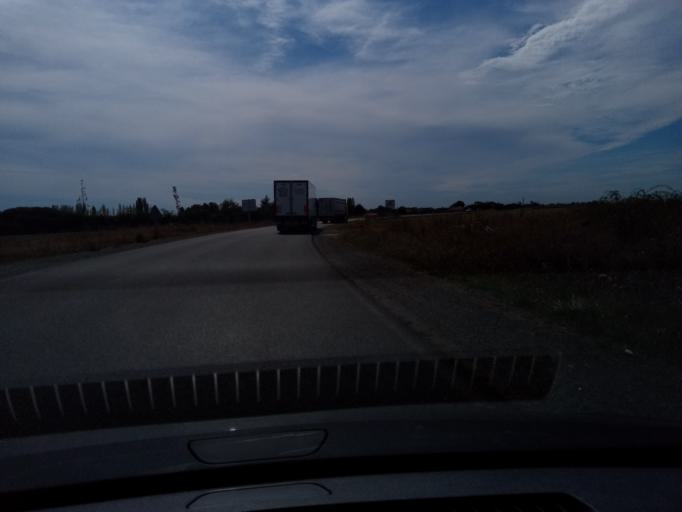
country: FR
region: Poitou-Charentes
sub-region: Departement de la Vienne
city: Terce
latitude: 46.4843
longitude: 0.5170
